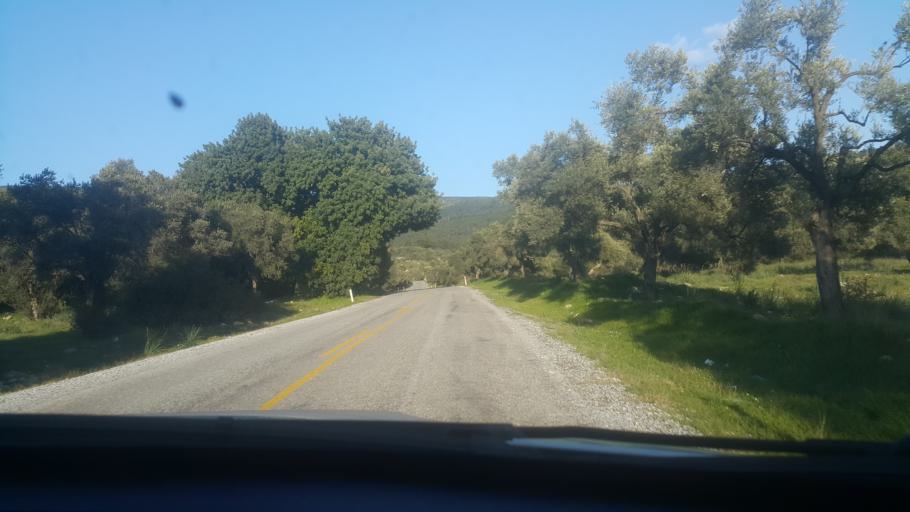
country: TR
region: Mugla
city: Kiulukioi
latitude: 37.3021
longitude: 27.6079
